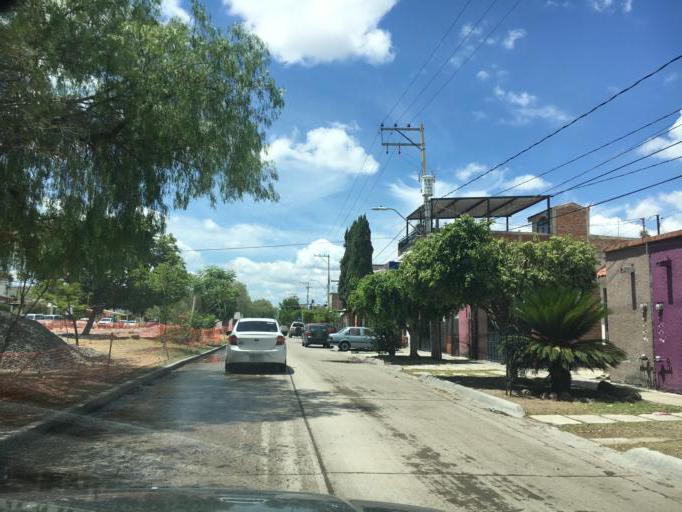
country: MX
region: Guanajuato
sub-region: Leon
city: San Jose de Duran (Los Troncoso)
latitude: 21.0789
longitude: -101.6446
